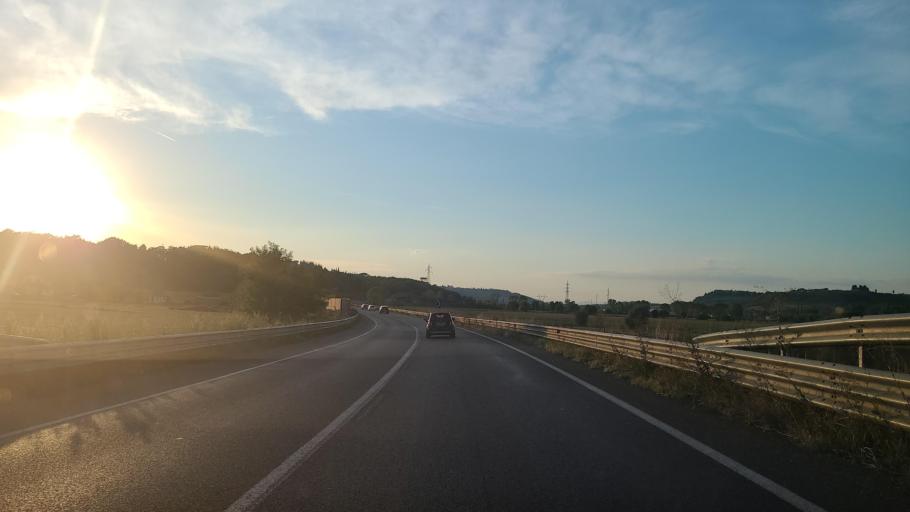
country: IT
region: Tuscany
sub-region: Provincia di Siena
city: Poggibonsi
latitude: 43.4849
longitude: 11.1187
